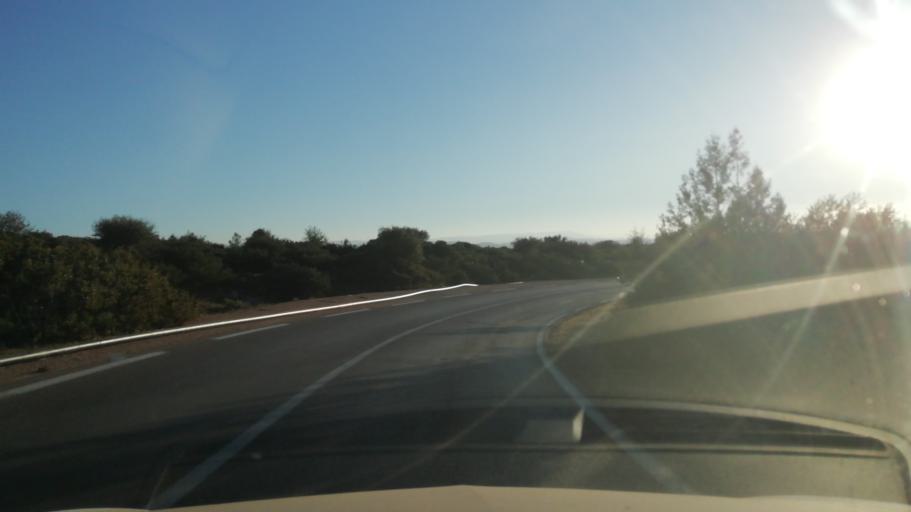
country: DZ
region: Tlemcen
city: Beni Mester
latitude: 34.8150
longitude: -1.6197
